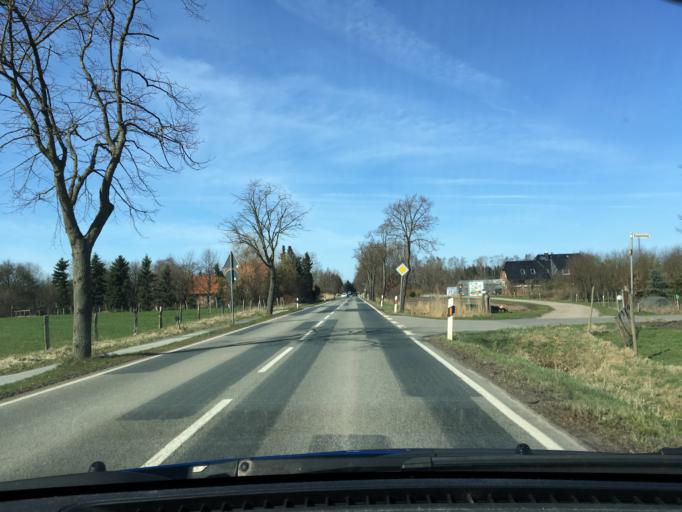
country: DE
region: Lower Saxony
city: Winsen
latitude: 53.3791
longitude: 10.2455
